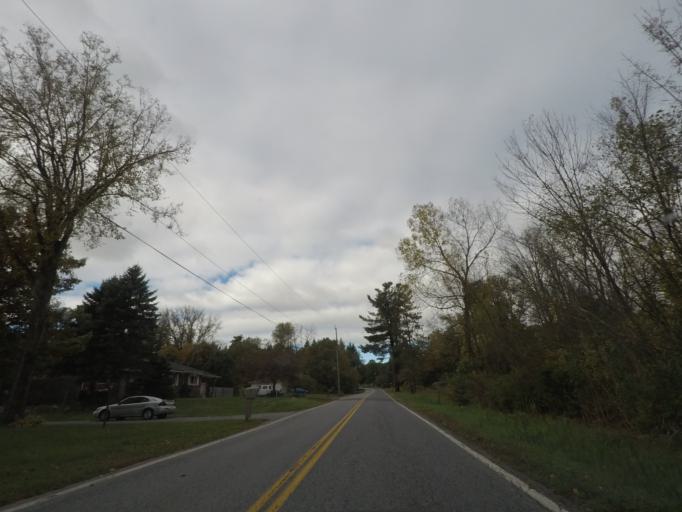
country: US
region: New York
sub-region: Saratoga County
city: Mechanicville
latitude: 42.8821
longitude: -73.7367
